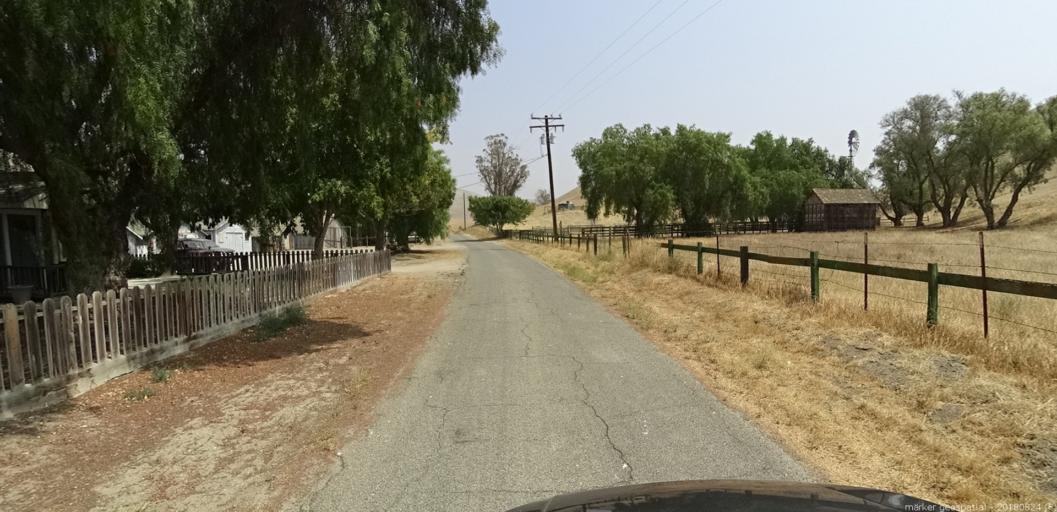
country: US
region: California
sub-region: Monterey County
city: King City
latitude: 36.1982
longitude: -121.0202
